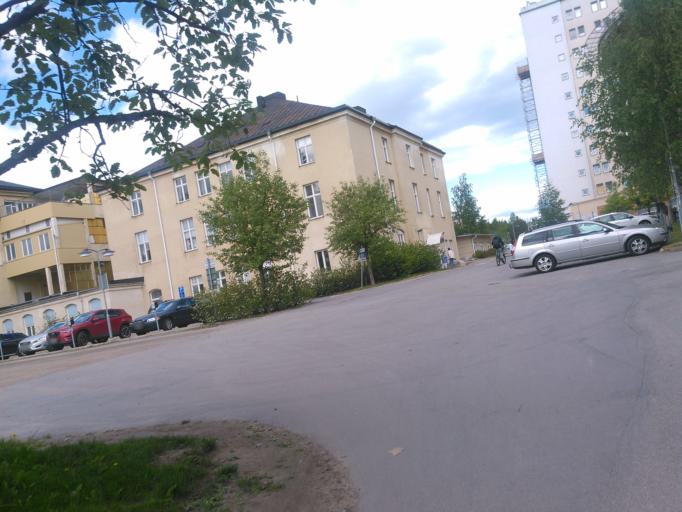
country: SE
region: Vaesterbotten
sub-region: Umea Kommun
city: Umea
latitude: 63.8162
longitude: 20.2976
